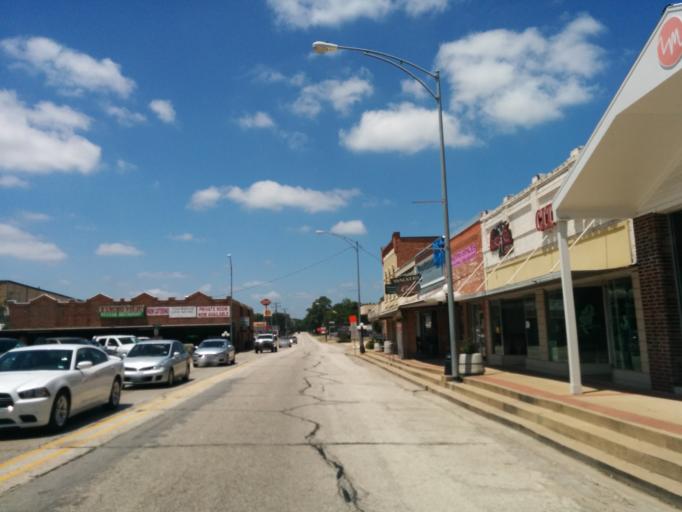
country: US
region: Texas
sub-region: Madison County
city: Madisonville
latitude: 30.9491
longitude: -95.9140
